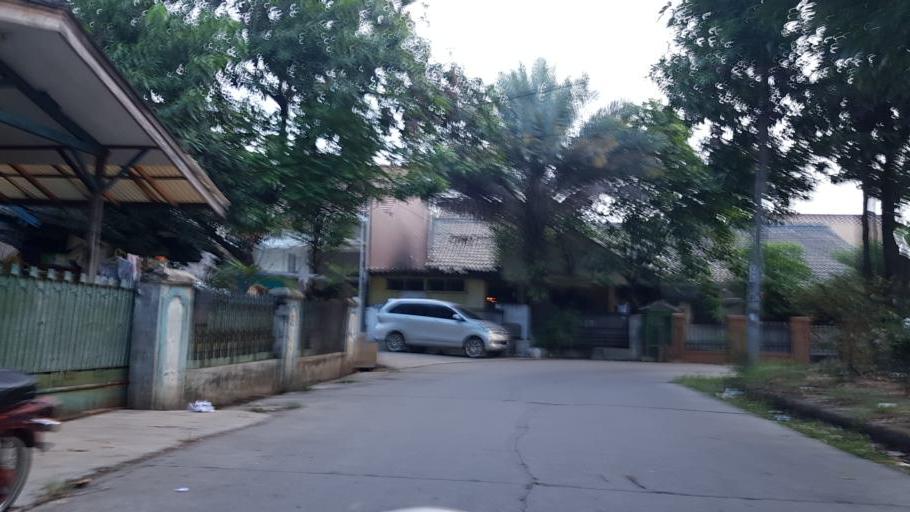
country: ID
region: West Java
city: Bekasi
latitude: -6.2676
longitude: 106.9477
